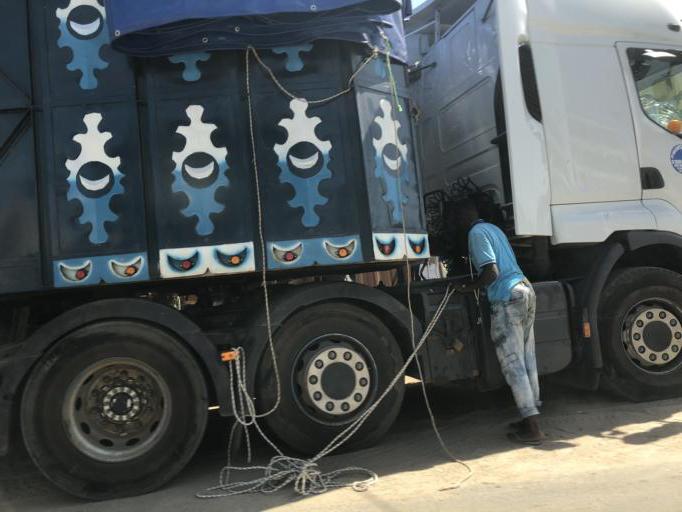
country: SN
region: Dakar
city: Mermoz Boabab
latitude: 14.7270
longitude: -17.4883
